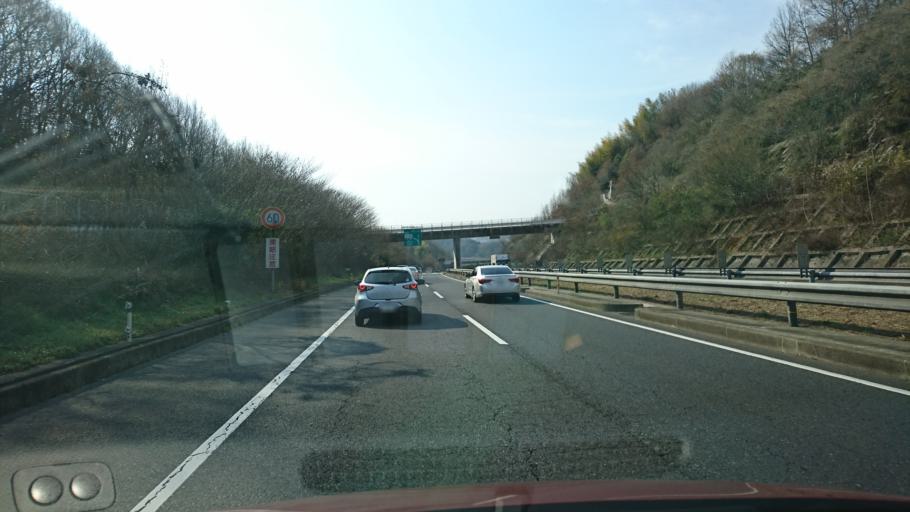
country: JP
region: Hiroshima
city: Onomichi
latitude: 34.4377
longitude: 133.2252
